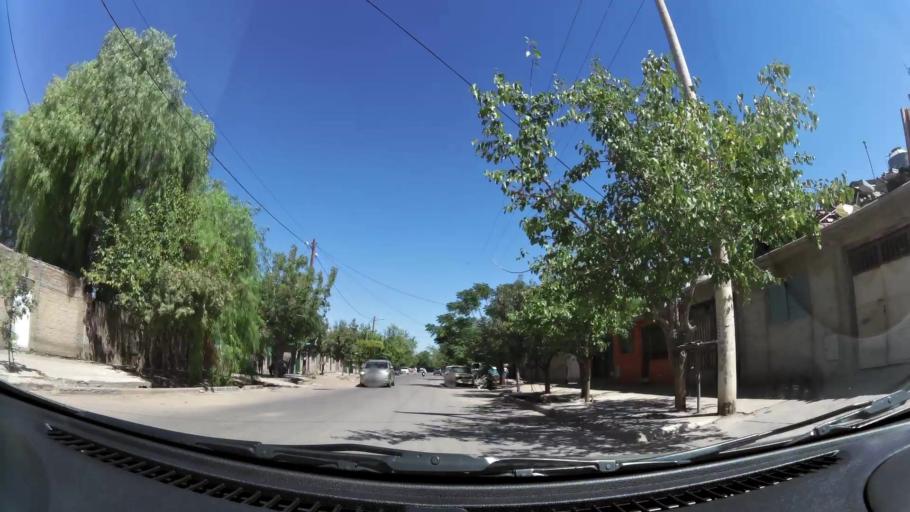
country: AR
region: Mendoza
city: Villa Nueva
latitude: -32.8791
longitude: -68.7979
